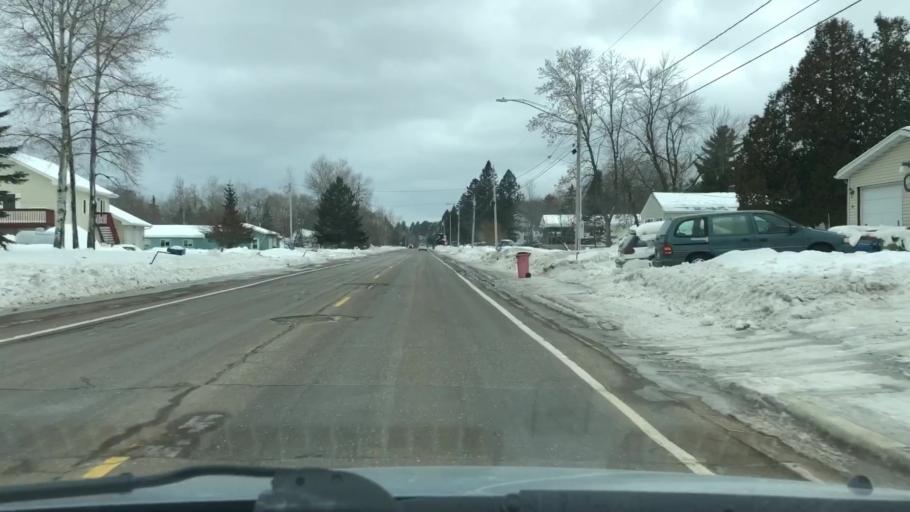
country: US
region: Minnesota
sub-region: Carlton County
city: Carlton
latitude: 46.6636
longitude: -92.3896
